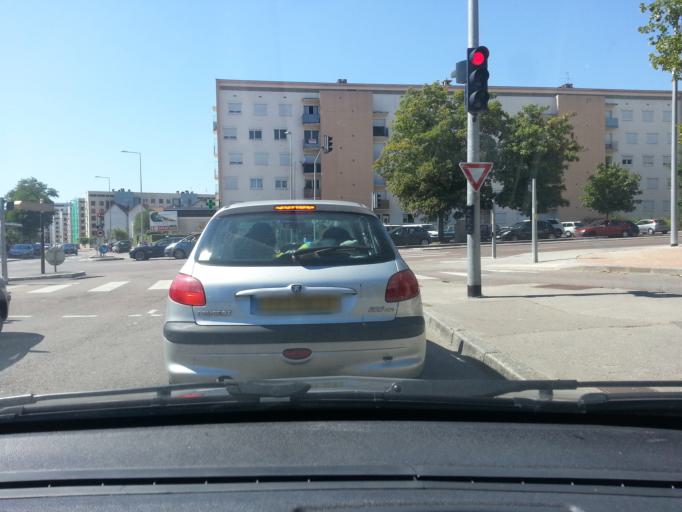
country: FR
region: Bourgogne
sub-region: Departement de la Cote-d'Or
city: Longvic
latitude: 47.3125
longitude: 5.0629
